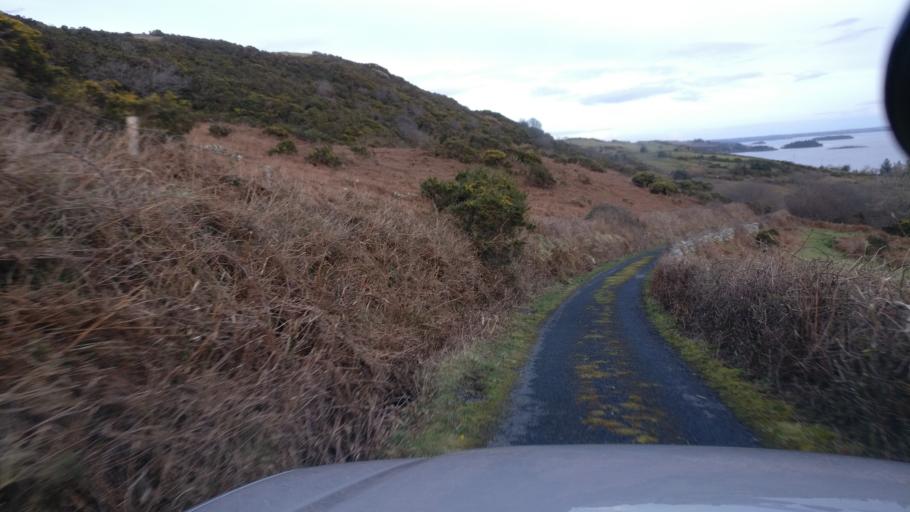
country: IE
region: Connaught
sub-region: County Galway
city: Oughterard
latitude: 53.5214
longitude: -9.4029
